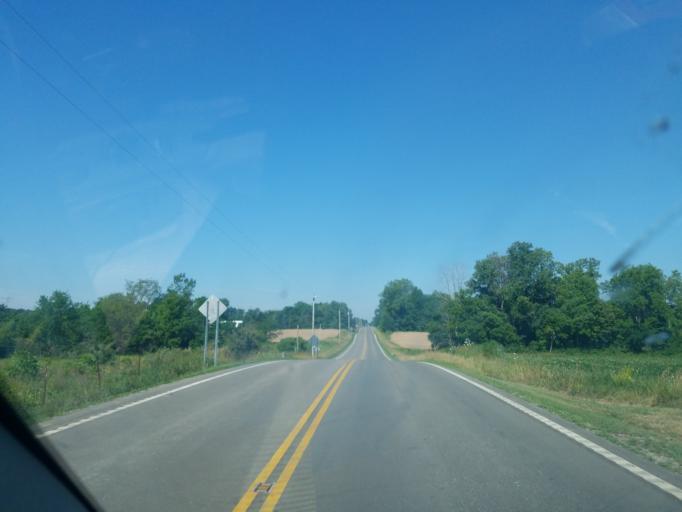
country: US
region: Ohio
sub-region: Logan County
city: Northwood
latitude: 40.4547
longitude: -83.7300
